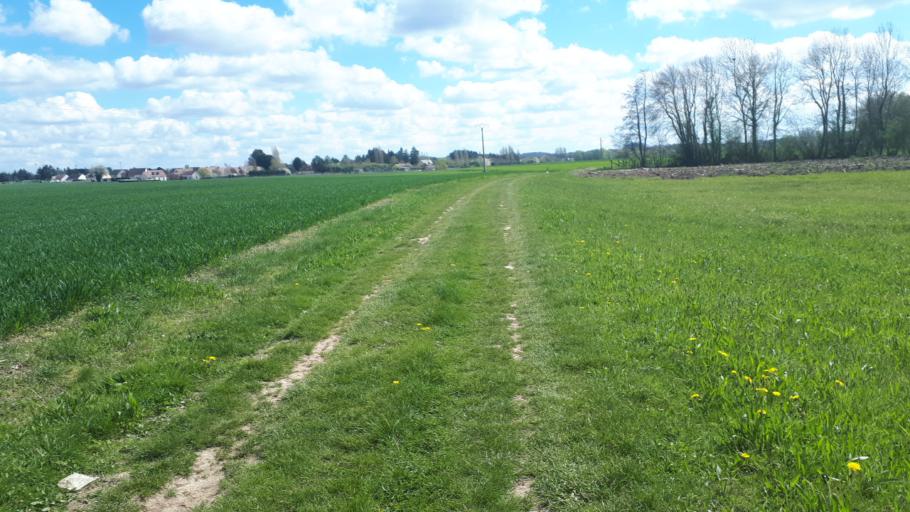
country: FR
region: Centre
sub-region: Departement du Loir-et-Cher
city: Villiers-sur-Loir
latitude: 47.7939
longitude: 0.9886
